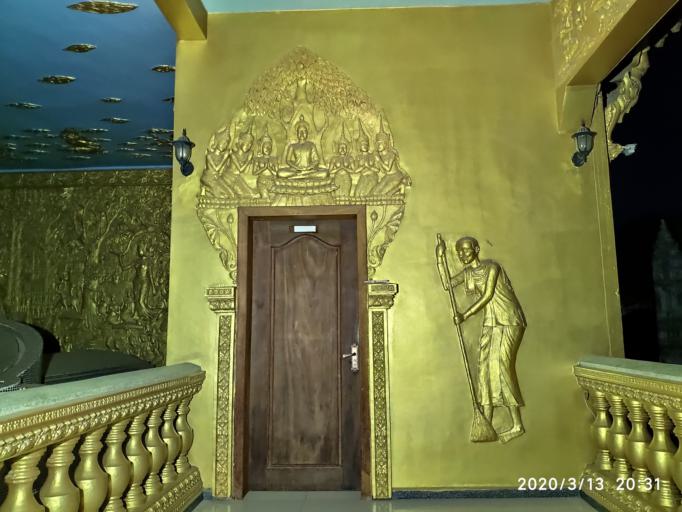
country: KH
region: Battambang
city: Battambang
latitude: 13.0933
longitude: 103.2018
